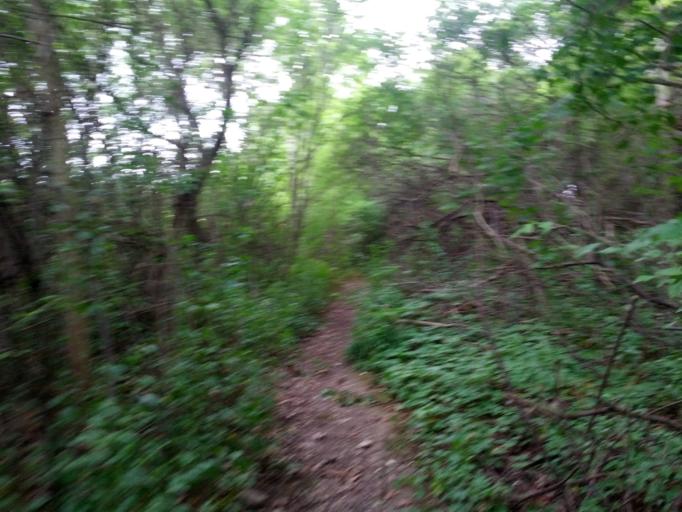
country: DE
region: Thuringia
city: Eisenach
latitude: 50.9850
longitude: 10.3331
